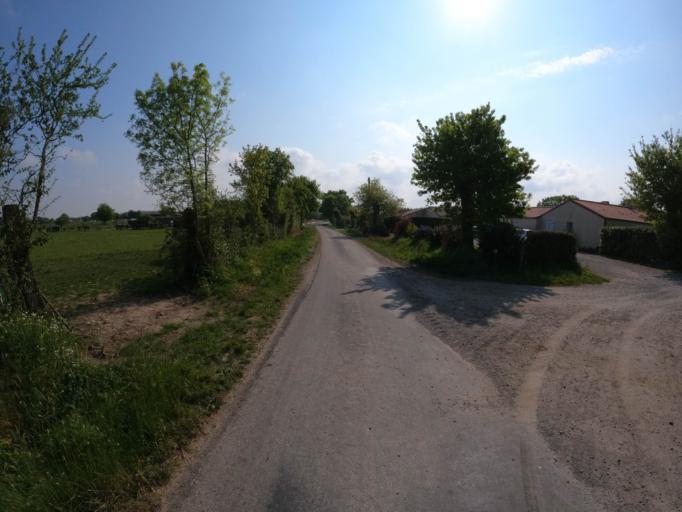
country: FR
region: Pays de la Loire
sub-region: Departement de la Vendee
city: La Bruffiere
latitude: 47.0084
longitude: -1.2096
